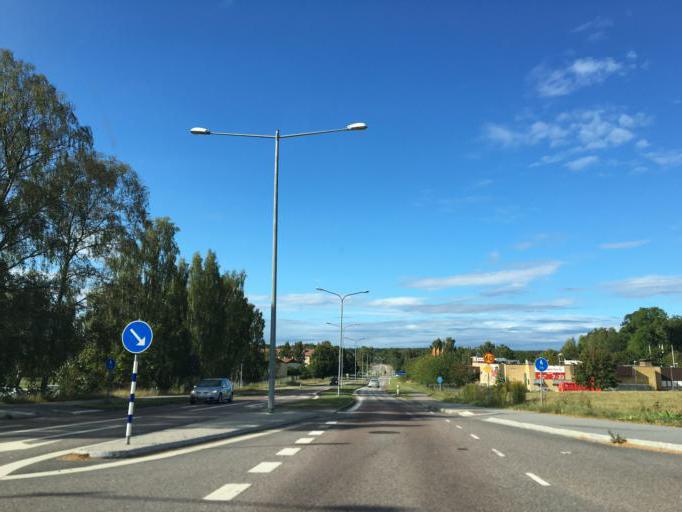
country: SE
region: Soedermanland
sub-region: Nykopings Kommun
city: Nykoping
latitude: 58.7672
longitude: 16.9881
